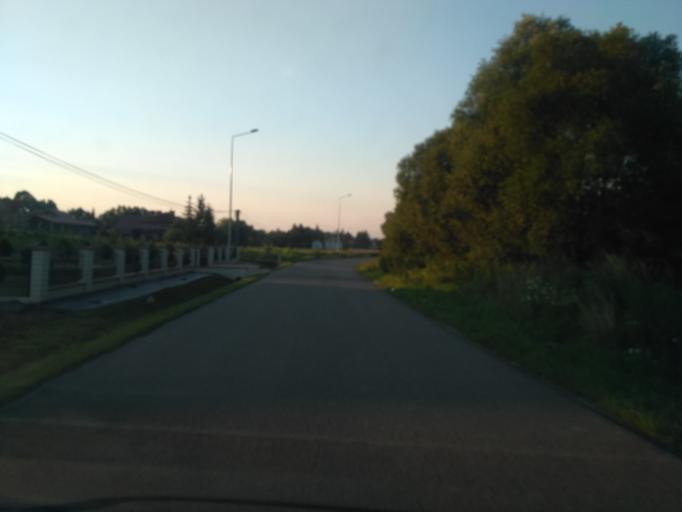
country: PL
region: Subcarpathian Voivodeship
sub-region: Powiat strzyzowski
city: Wysoka Strzyzowska
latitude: 49.8184
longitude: 21.7417
